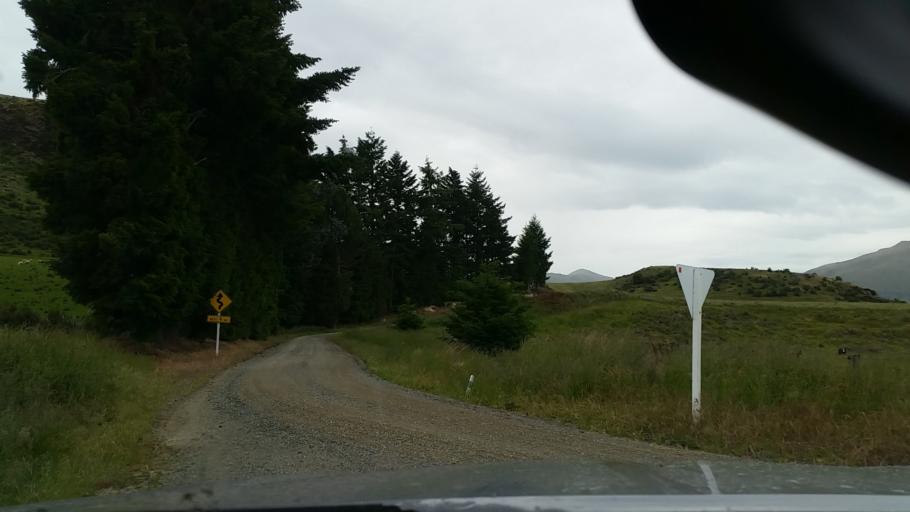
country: NZ
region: Otago
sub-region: Queenstown-Lakes District
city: Kingston
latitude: -45.4531
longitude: 168.7129
